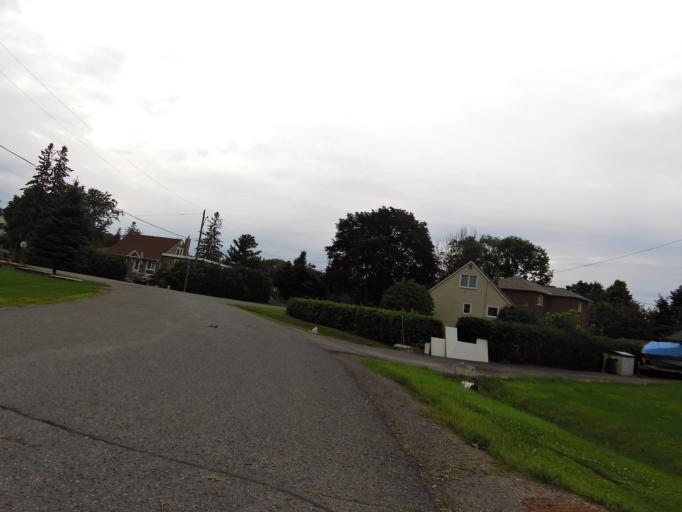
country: CA
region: Ontario
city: Ottawa
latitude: 45.3504
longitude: -75.7361
